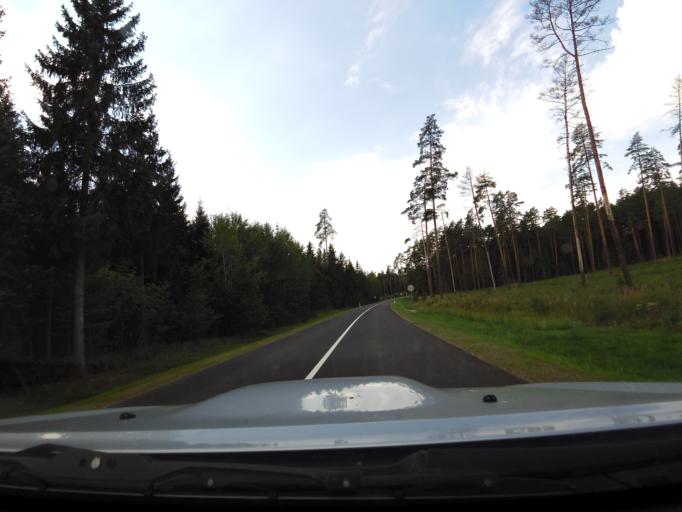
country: LT
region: Vilnius County
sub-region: Vilniaus Rajonas
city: Vievis
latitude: 54.8742
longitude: 24.7958
